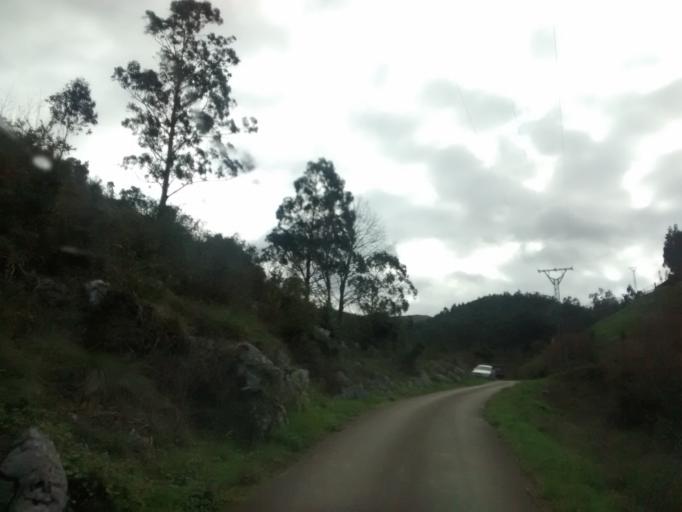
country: ES
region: Cantabria
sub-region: Provincia de Cantabria
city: Lierganes
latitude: 43.3371
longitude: -3.7044
